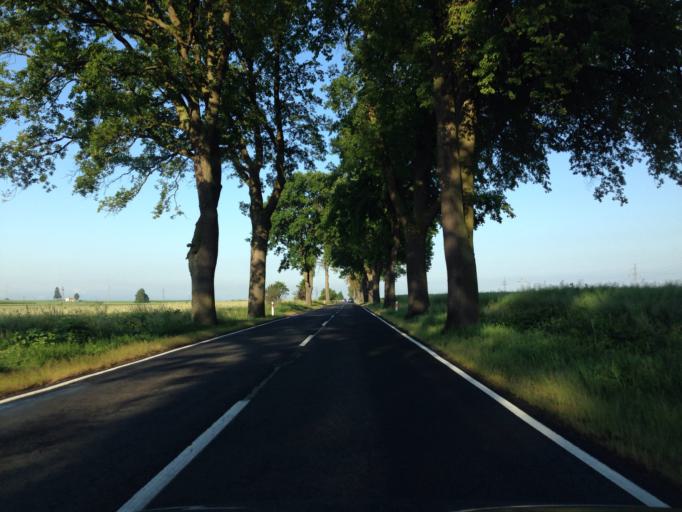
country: PL
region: Kujawsko-Pomorskie
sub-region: Powiat grudziadzki
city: Rogozno
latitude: 53.5774
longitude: 18.8838
